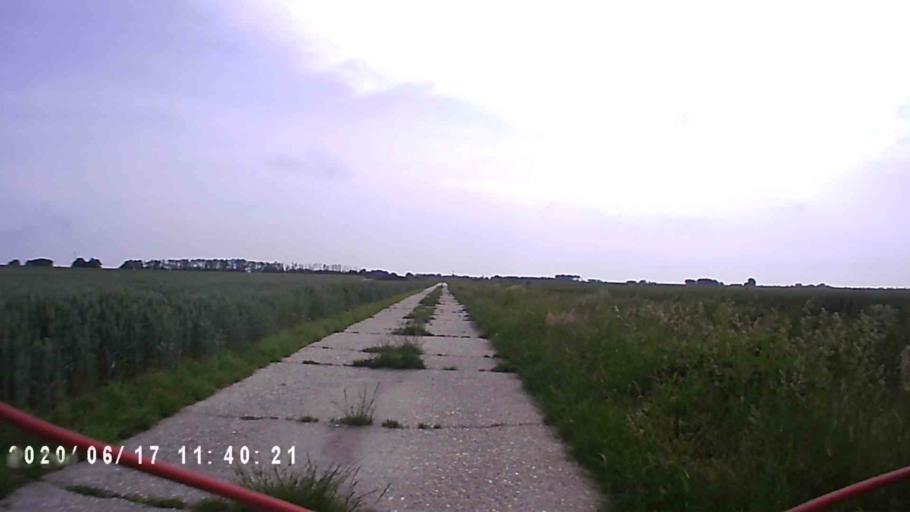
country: NL
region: Groningen
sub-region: Gemeente De Marne
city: Ulrum
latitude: 53.3616
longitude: 6.2741
